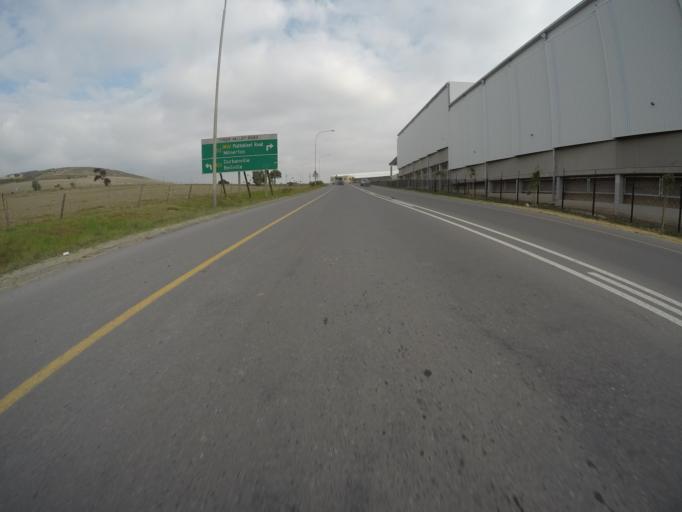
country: ZA
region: Western Cape
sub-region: City of Cape Town
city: Sunset Beach
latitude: -33.8205
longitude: 18.5577
